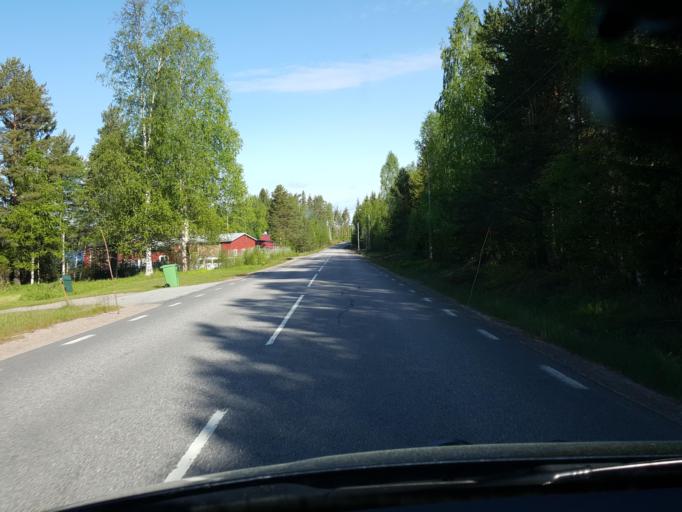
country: SE
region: Vaesternorrland
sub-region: Ange Kommun
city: Ange
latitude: 62.1730
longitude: 15.6682
